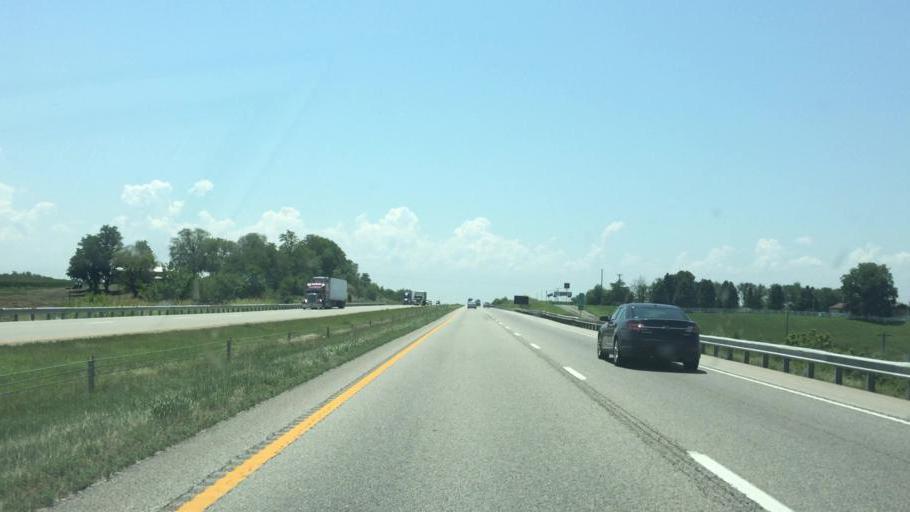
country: US
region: Kansas
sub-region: Doniphan County
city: Elwood
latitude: 39.6102
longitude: -94.7885
